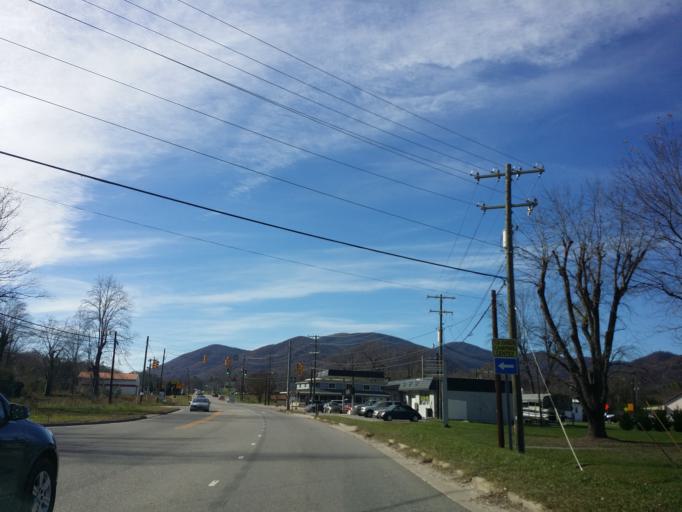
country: US
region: North Carolina
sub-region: McDowell County
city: West Marion
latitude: 35.6922
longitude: -82.0609
